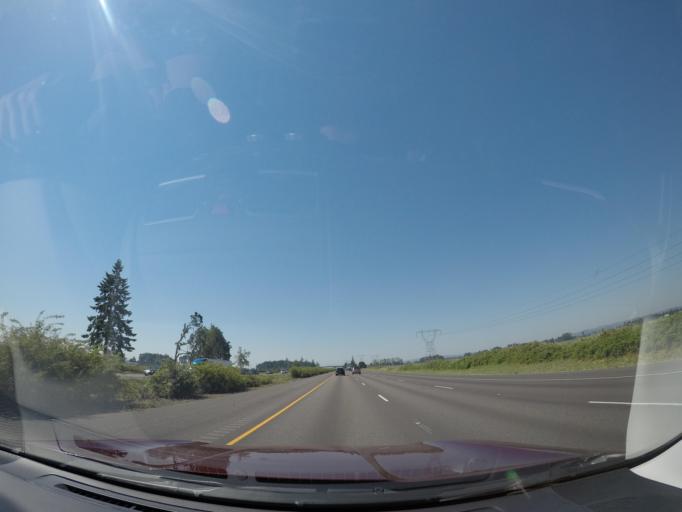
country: US
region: Oregon
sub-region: Marion County
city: Gervais
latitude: 45.0794
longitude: -122.9537
